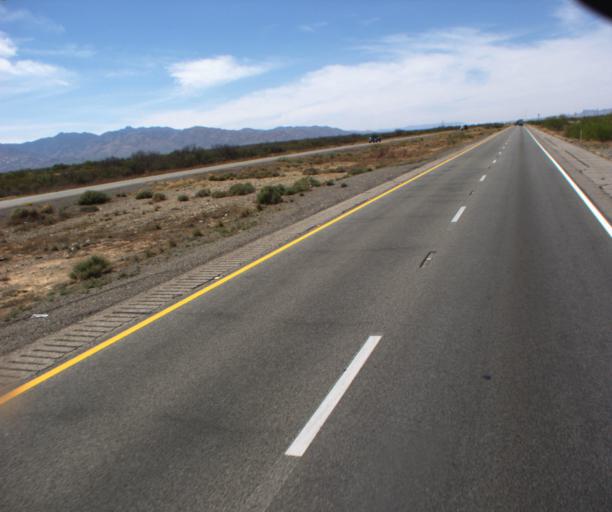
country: US
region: Arizona
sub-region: Cochise County
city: Willcox
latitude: 32.3002
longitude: -109.3657
